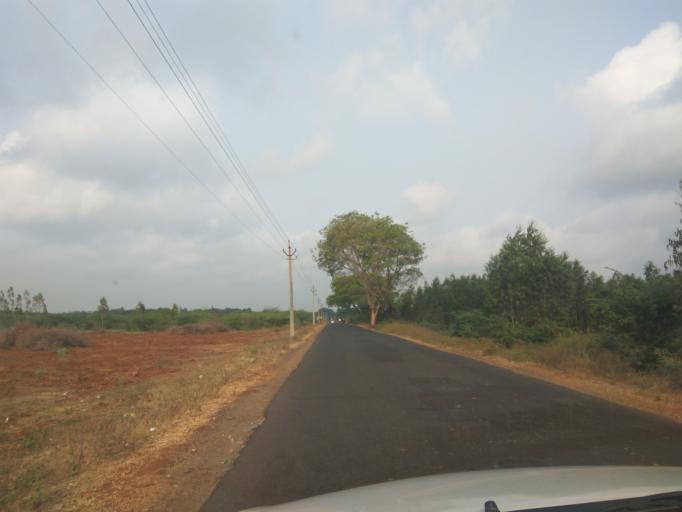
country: IN
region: Andhra Pradesh
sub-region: Prakasam
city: Kandukur
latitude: 15.2094
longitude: 79.8803
